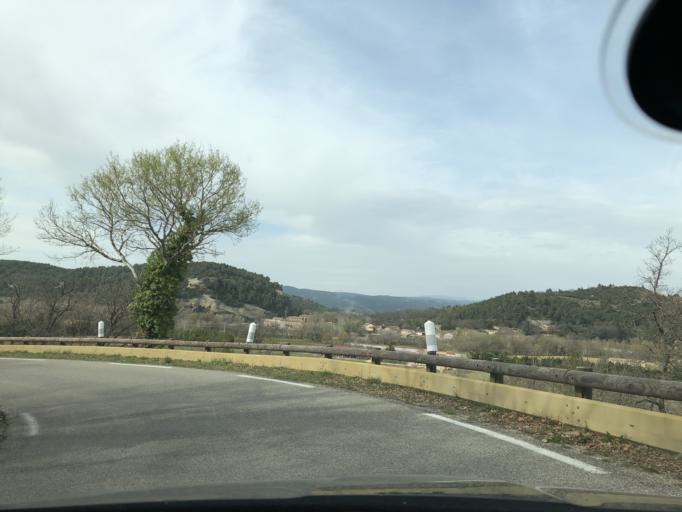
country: FR
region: Provence-Alpes-Cote d'Azur
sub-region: Departement du Vaucluse
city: Goult
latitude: 43.8515
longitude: 5.2337
